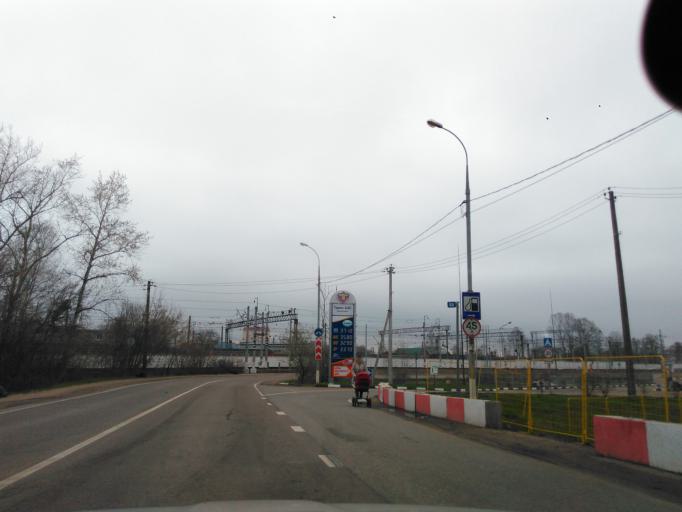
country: RU
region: Moskovskaya
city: Nakhabino
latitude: 55.8438
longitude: 37.1723
